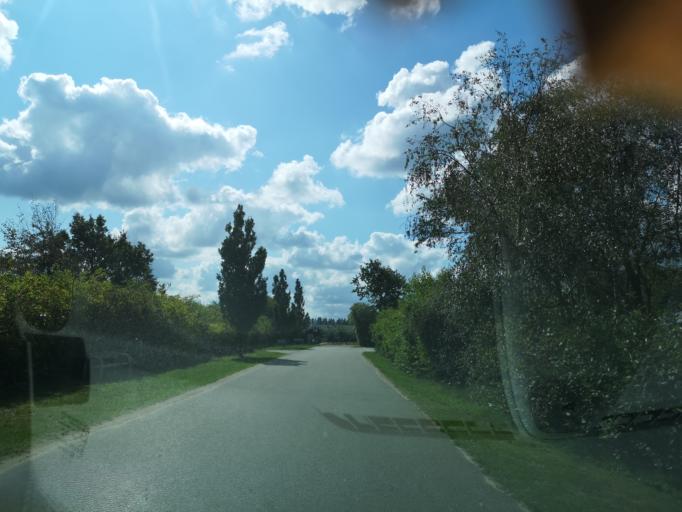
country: DK
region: Central Jutland
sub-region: Ringkobing-Skjern Kommune
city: Skjern
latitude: 55.8866
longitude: 8.3581
